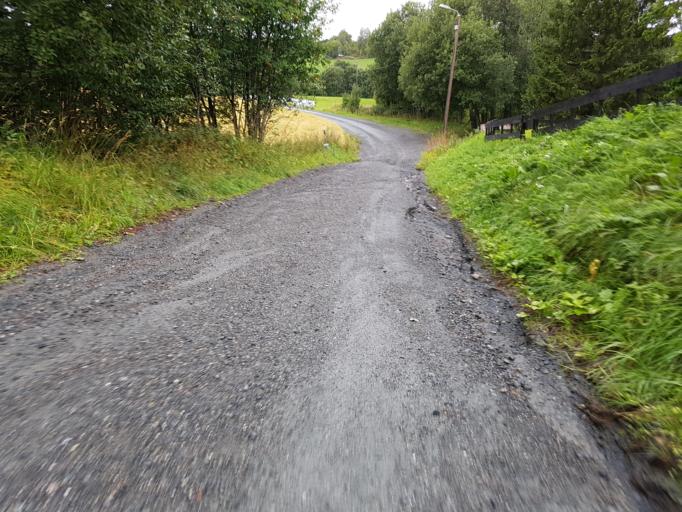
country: NO
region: Sor-Trondelag
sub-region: Trondheim
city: Trondheim
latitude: 63.3995
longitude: 10.4654
